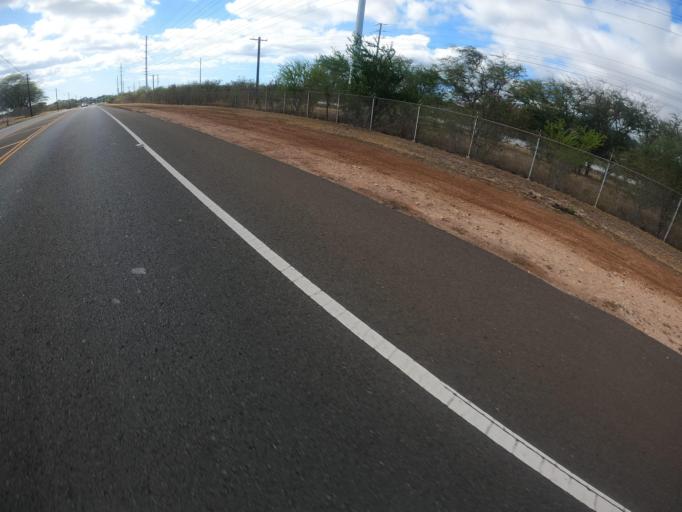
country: US
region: Hawaii
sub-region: Honolulu County
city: Makakilo City
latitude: 21.3242
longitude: -158.0696
